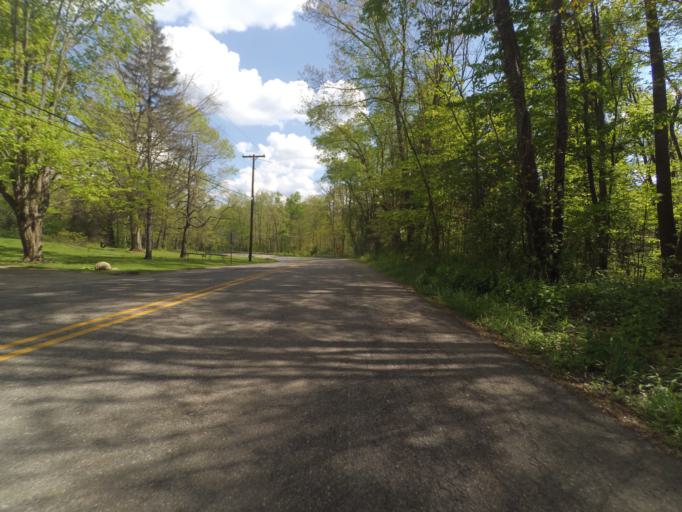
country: US
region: Ohio
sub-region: Mahoning County
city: Austintown
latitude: 41.1221
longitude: -80.7367
